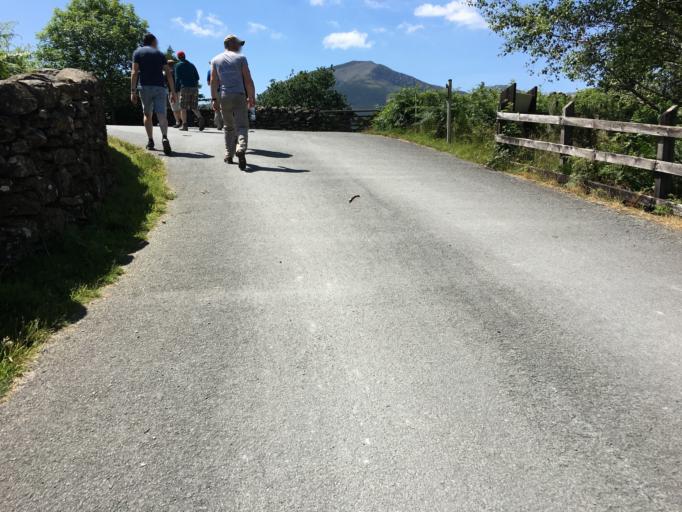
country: GB
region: Wales
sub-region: Gwynedd
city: Penrhyndeudraeth
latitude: 53.0195
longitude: -4.0822
